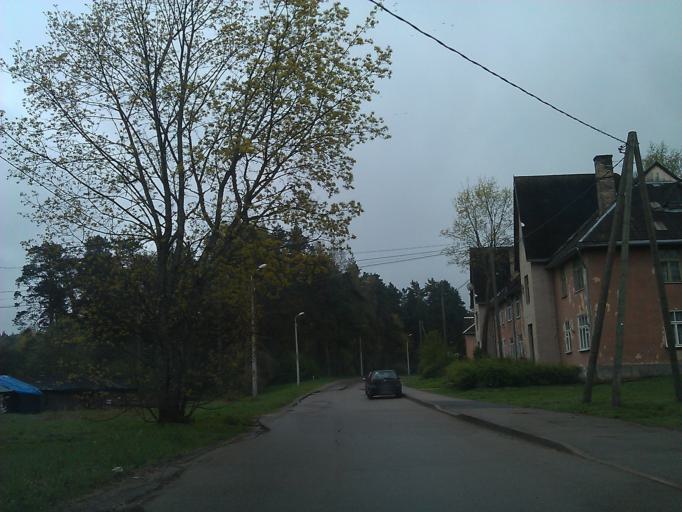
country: LV
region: Stopini
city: Ulbroka
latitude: 56.9621
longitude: 24.3003
